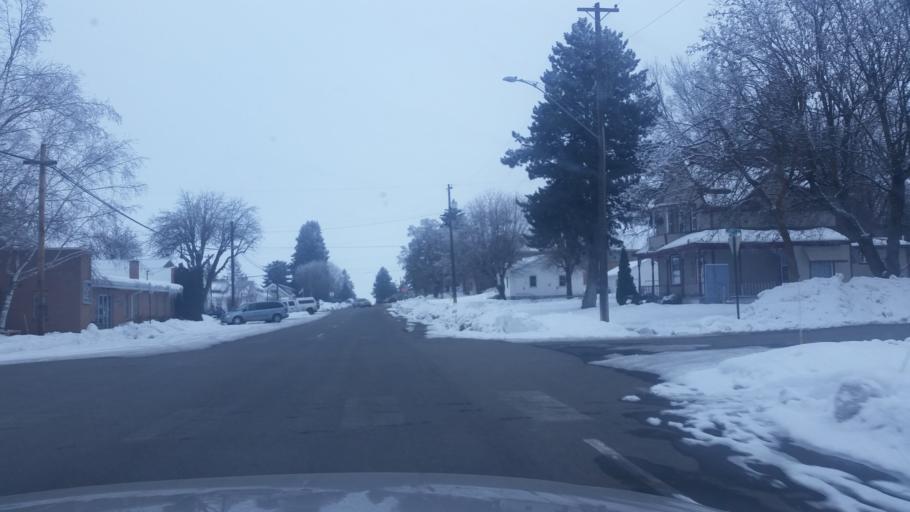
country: US
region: Washington
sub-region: Spokane County
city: Medical Lake
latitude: 47.6684
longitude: -117.8795
